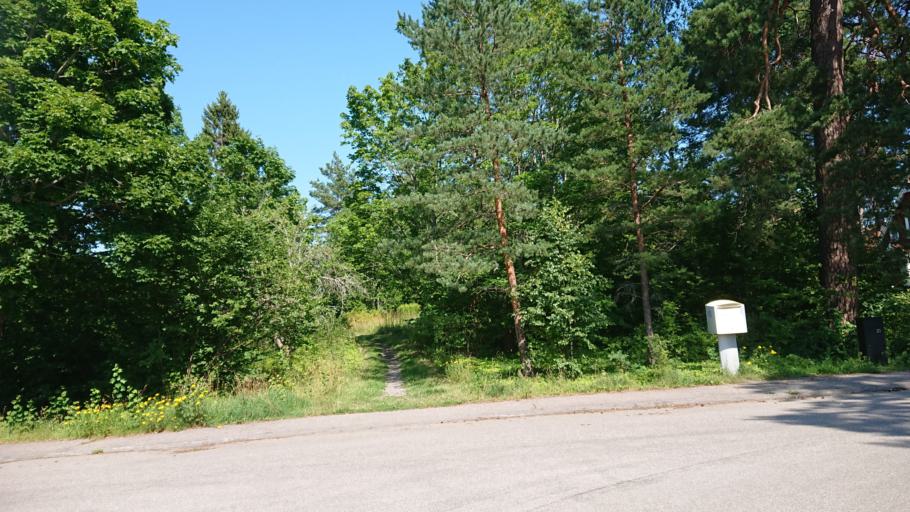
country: SE
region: Uppsala
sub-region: Osthammars Kommun
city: Osterbybruk
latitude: 60.1981
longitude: 17.9042
